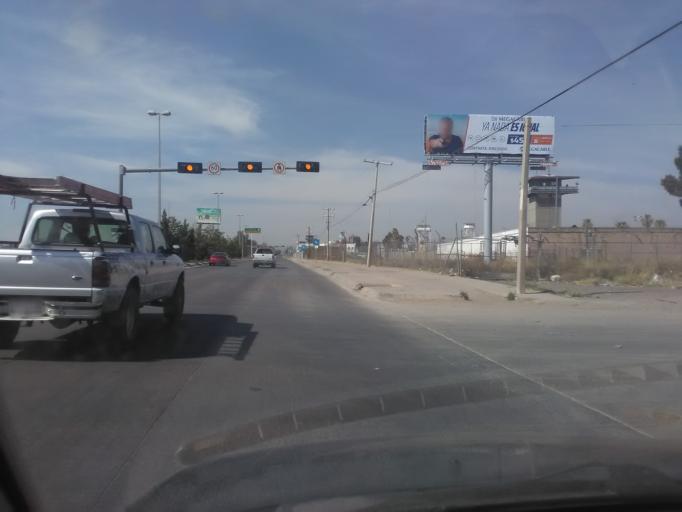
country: MX
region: Durango
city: Victoria de Durango
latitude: 24.0729
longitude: -104.5952
